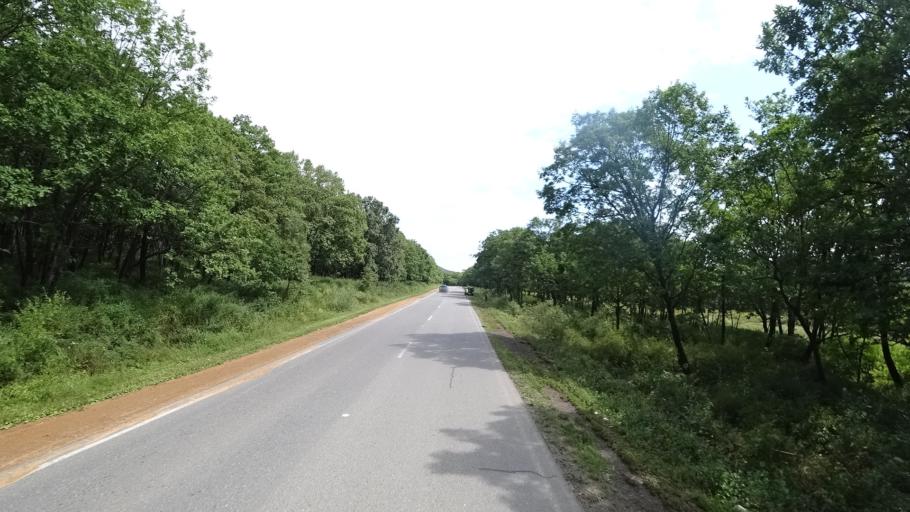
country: RU
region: Primorskiy
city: Lyalichi
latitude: 44.1408
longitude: 132.4096
